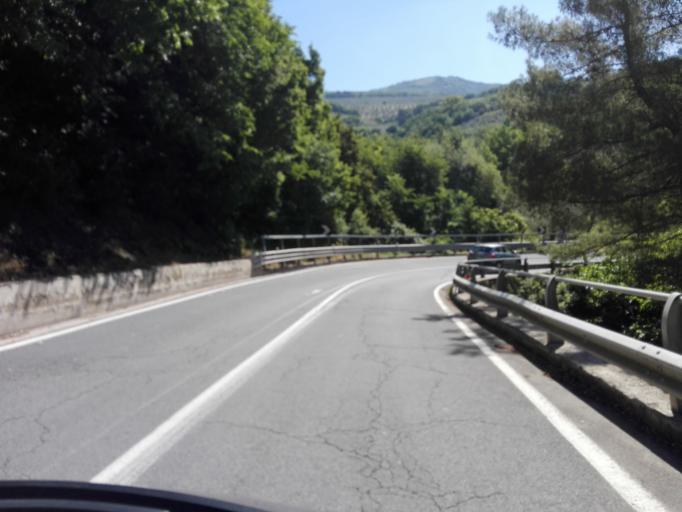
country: IT
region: Umbria
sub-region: Provincia di Perugia
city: Foligno
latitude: 42.9654
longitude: 12.7476
